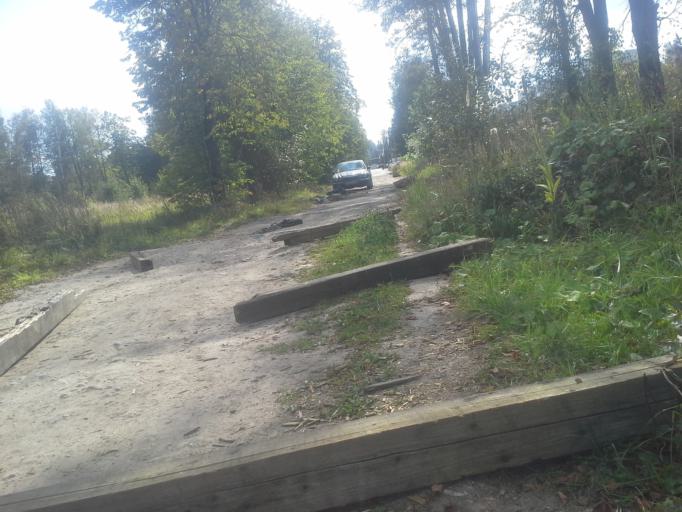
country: RU
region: Moskovskaya
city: Selyatino
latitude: 55.4814
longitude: 37.0023
